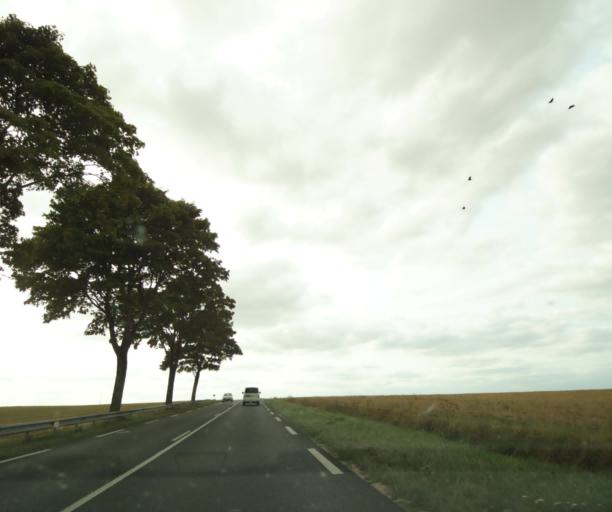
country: FR
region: Centre
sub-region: Departement d'Indre-et-Loire
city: Chambourg-sur-Indre
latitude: 47.1850
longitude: 0.9465
